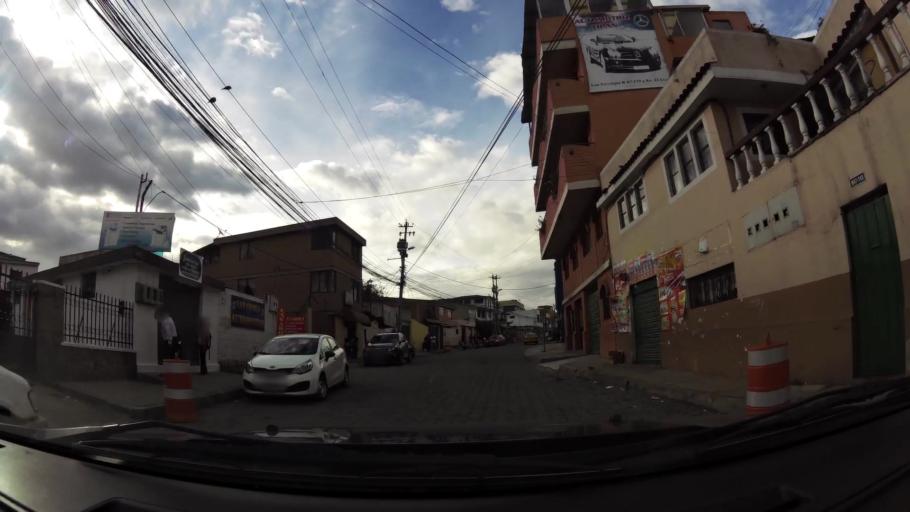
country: EC
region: Pichincha
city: Quito
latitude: -0.1528
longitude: -78.4727
